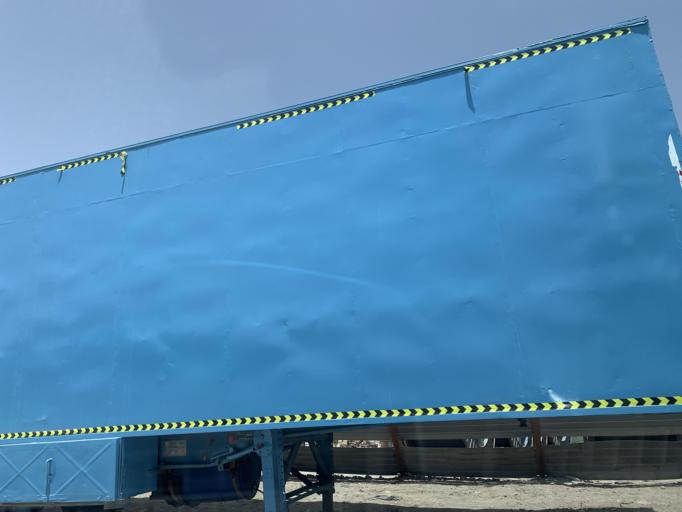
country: BH
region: Northern
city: Sitrah
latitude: 26.1742
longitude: 50.6046
